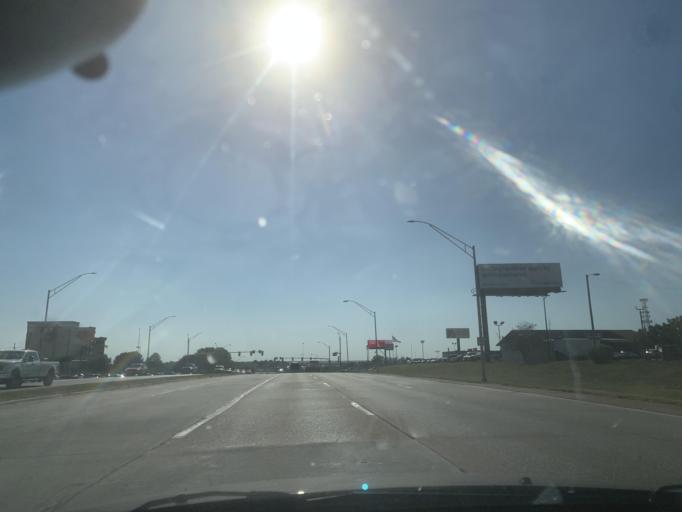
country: US
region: Nebraska
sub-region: Douglas County
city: Ralston
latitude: 41.2126
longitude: -96.0792
